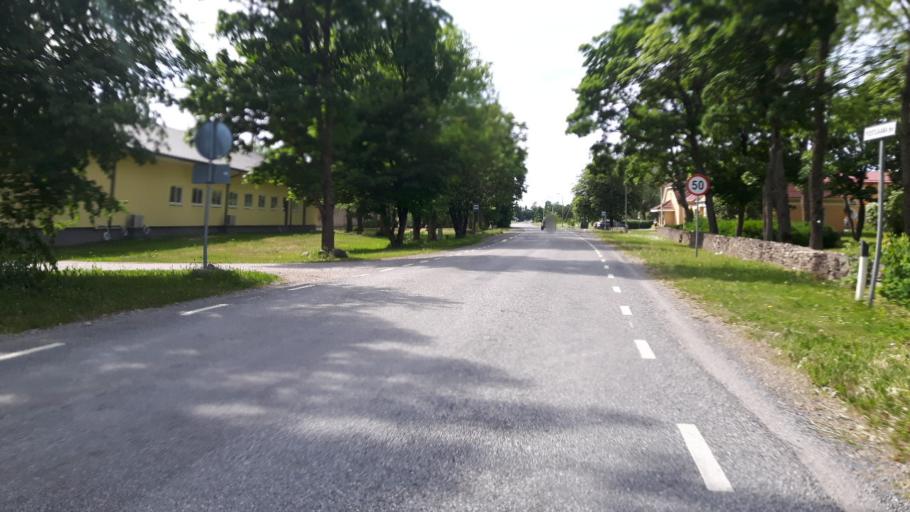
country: EE
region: Harju
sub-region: Raasiku vald
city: Raasiku
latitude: 59.4396
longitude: 25.1467
